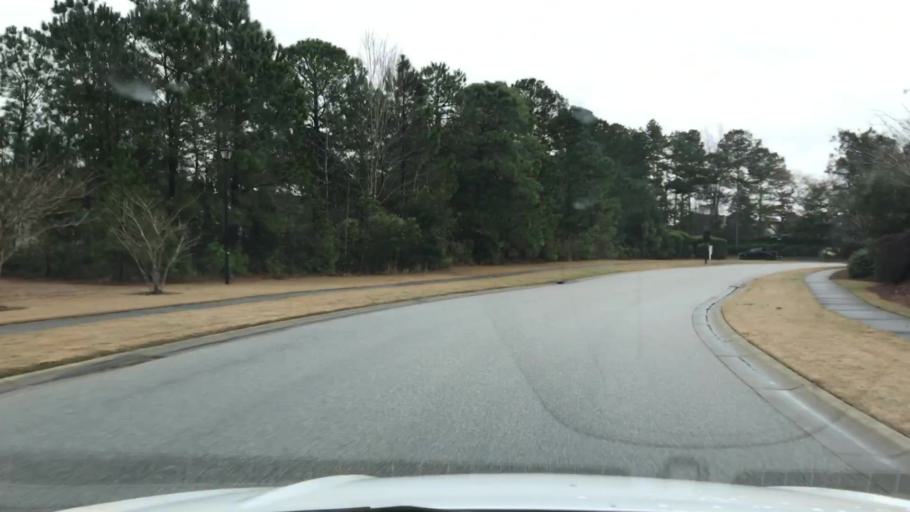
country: US
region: South Carolina
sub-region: Horry County
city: Myrtle Beach
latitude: 33.7458
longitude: -78.9034
